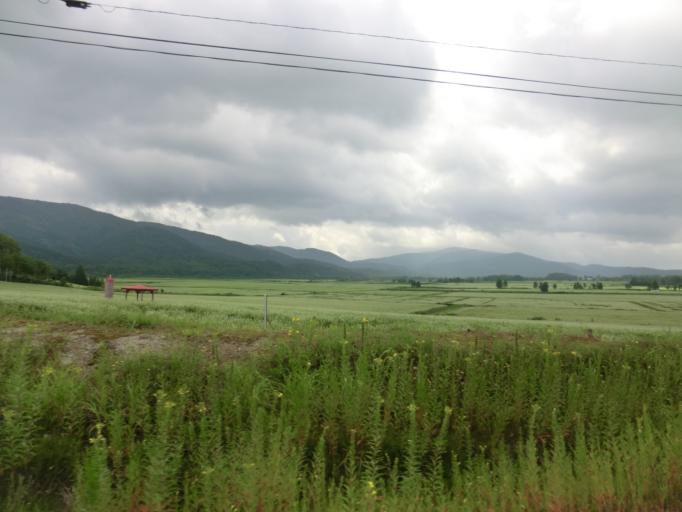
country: JP
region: Hokkaido
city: Nayoro
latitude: 44.1607
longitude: 142.1492
